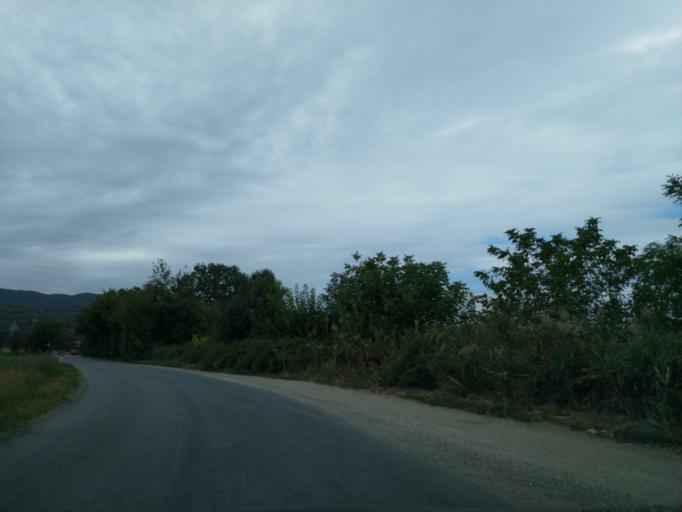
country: RS
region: Central Serbia
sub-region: Pomoravski Okrug
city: Paracin
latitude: 43.8319
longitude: 21.3327
